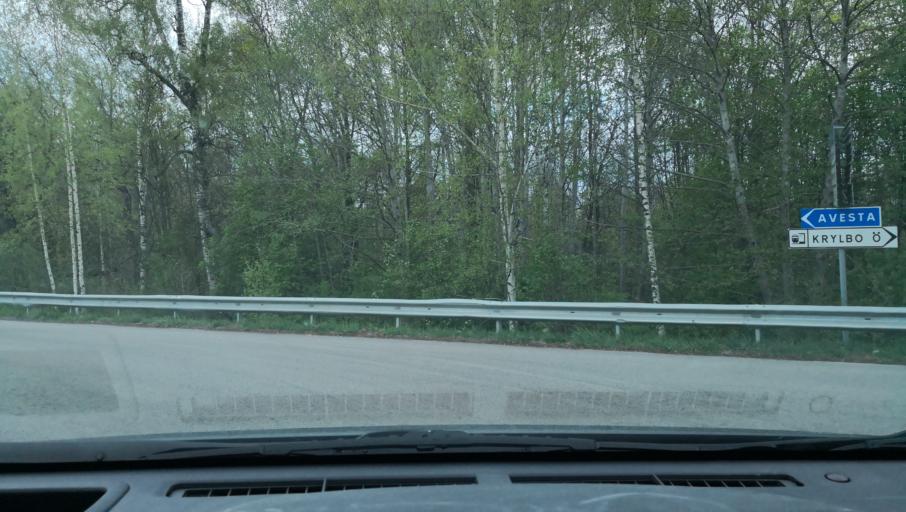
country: SE
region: Dalarna
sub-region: Avesta Kommun
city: Avesta
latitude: 60.1359
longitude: 16.2104
